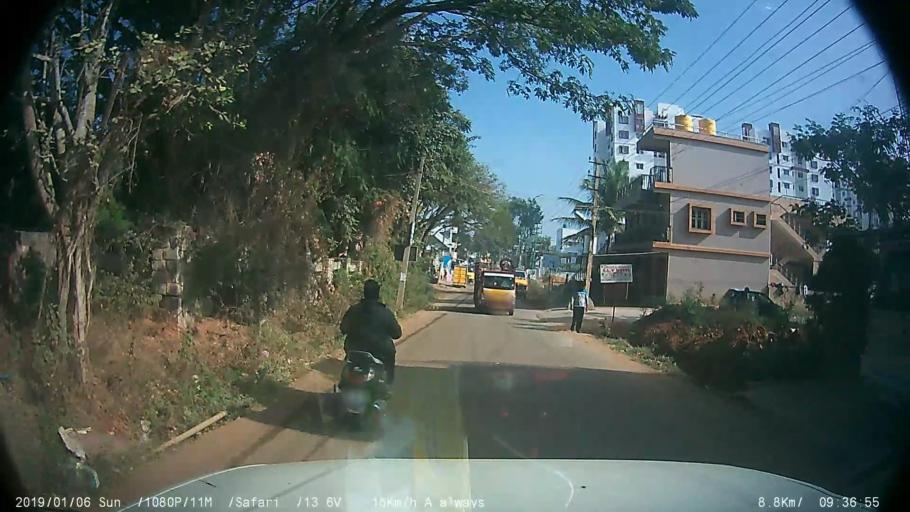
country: IN
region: Karnataka
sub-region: Bangalore Urban
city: Anekal
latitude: 12.8268
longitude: 77.6547
